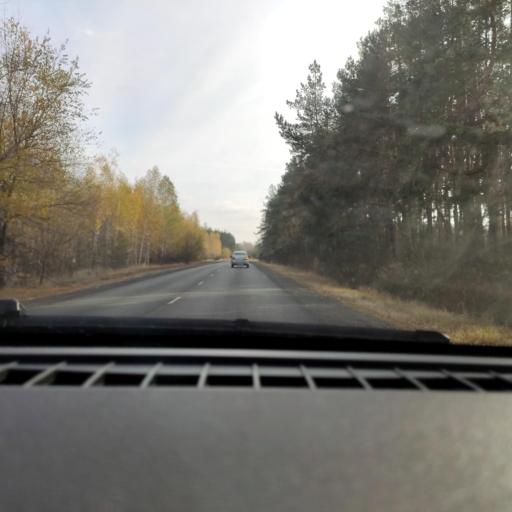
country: RU
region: Voronezj
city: Maslovka
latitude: 51.5796
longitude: 39.2872
